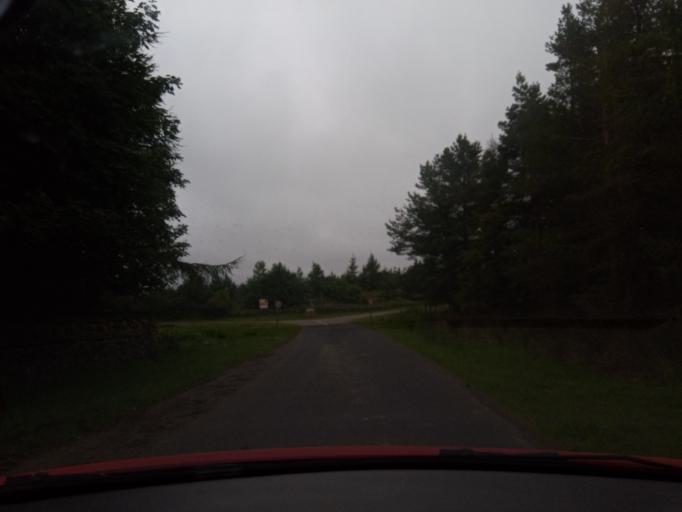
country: GB
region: England
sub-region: Northumberland
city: Otterburn
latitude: 55.2629
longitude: -2.1175
